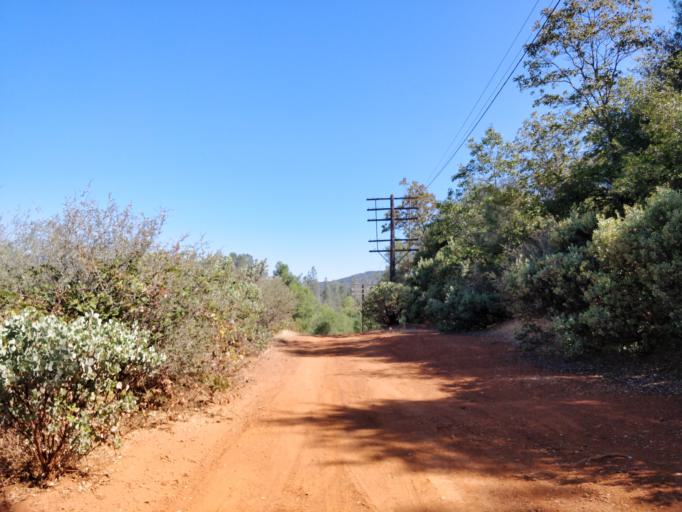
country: US
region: California
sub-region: Shasta County
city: Central Valley (historical)
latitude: 40.6690
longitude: -122.3942
